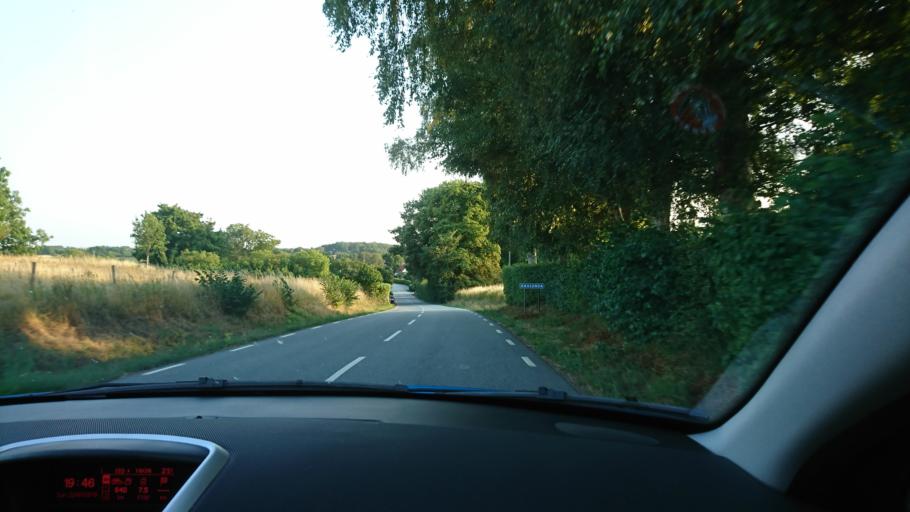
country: SE
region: Skane
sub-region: Simrishamns Kommun
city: Kivik
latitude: 55.7133
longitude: 14.1538
